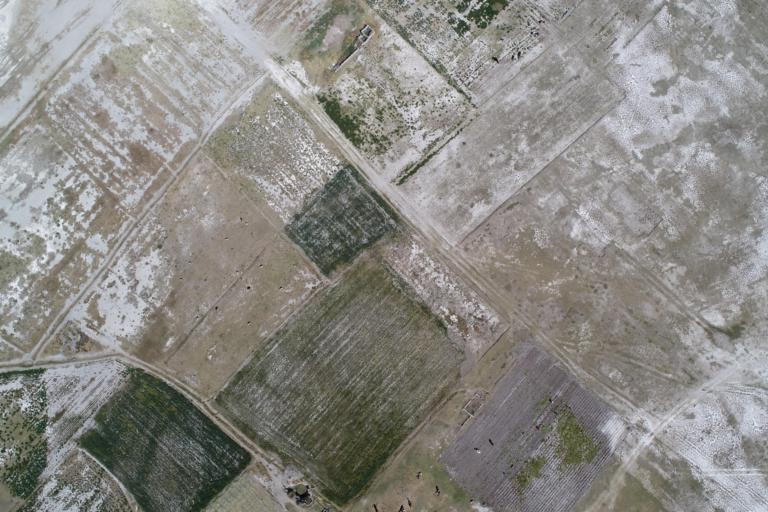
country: BO
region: La Paz
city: Achacachi
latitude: -16.0122
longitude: -68.7274
